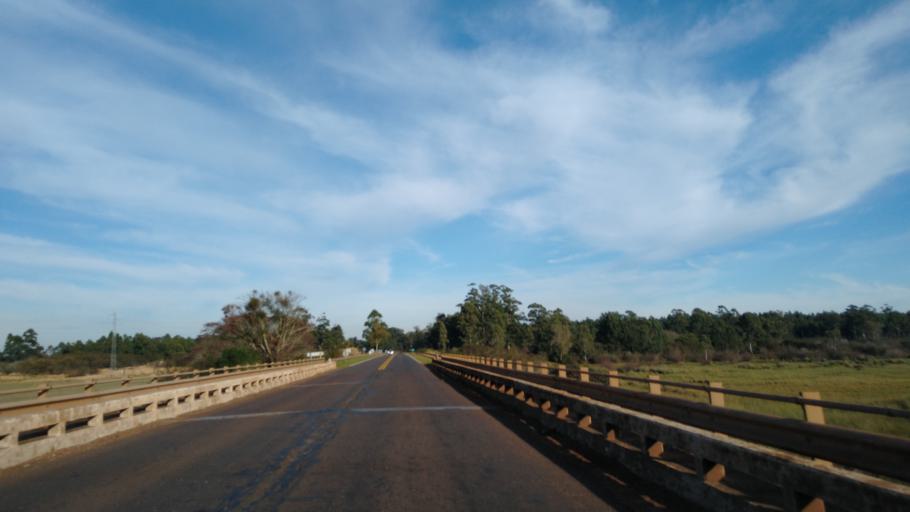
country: AR
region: Corrientes
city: Yapeyu
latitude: -29.4235
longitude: -56.8535
